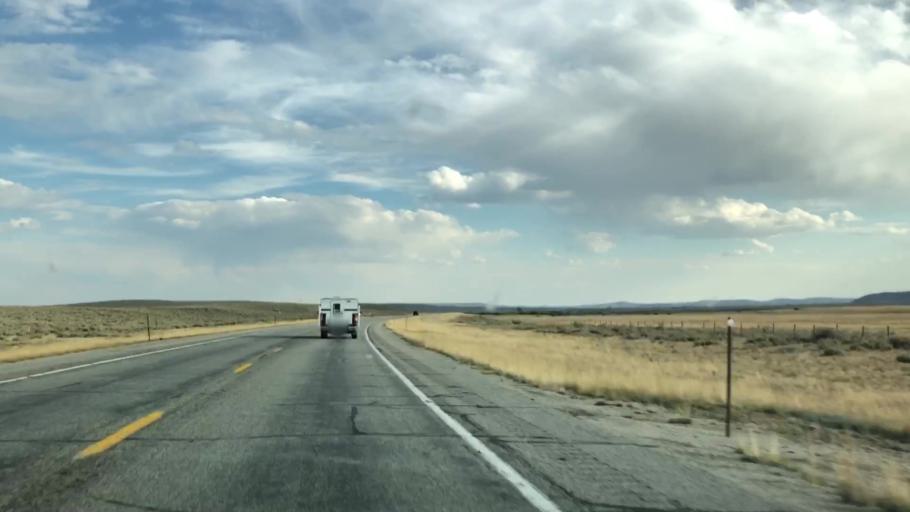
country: US
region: Wyoming
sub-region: Sublette County
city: Pinedale
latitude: 43.0317
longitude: -110.1282
